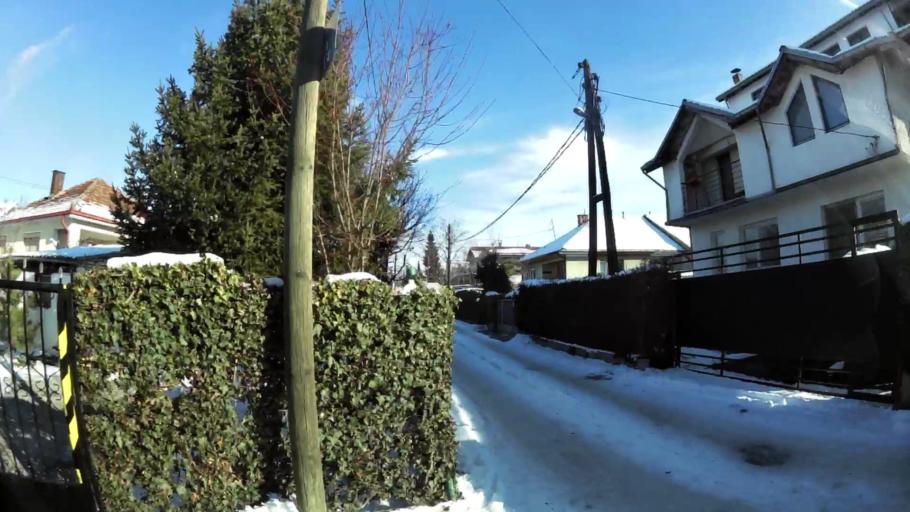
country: MK
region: Saraj
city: Saraj
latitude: 42.0060
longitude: 21.3379
